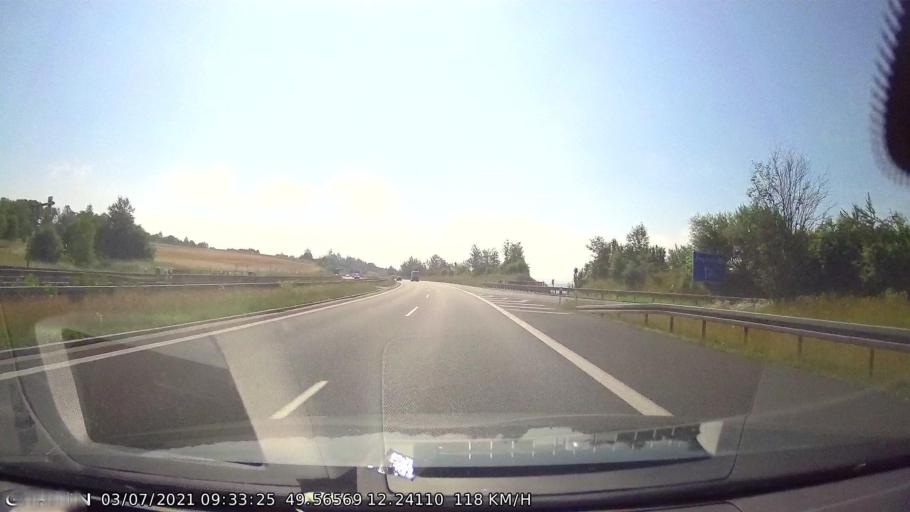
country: DE
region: Bavaria
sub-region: Upper Palatinate
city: Leuchtenberg
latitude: 49.5655
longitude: 12.2405
